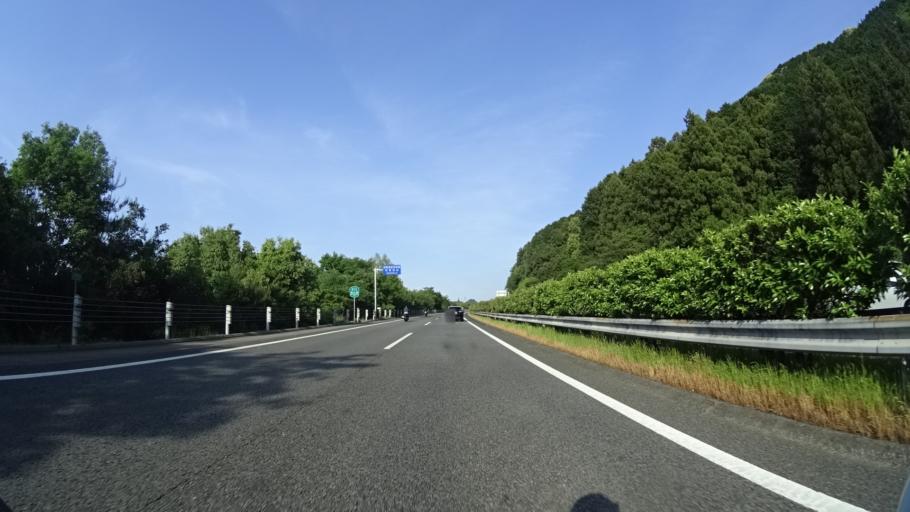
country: JP
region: Ehime
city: Niihama
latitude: 33.9285
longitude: 133.3337
